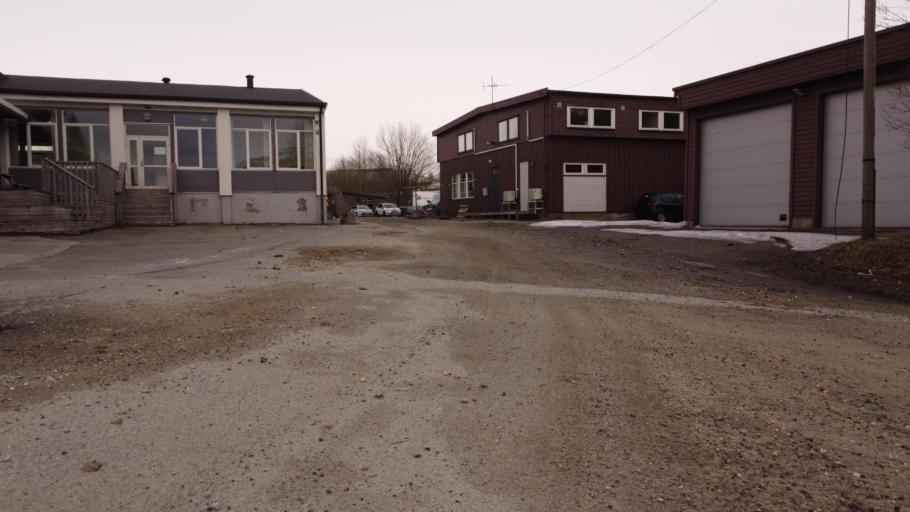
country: NO
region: Nordland
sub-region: Rana
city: Mo i Rana
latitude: 66.3089
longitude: 14.1479
